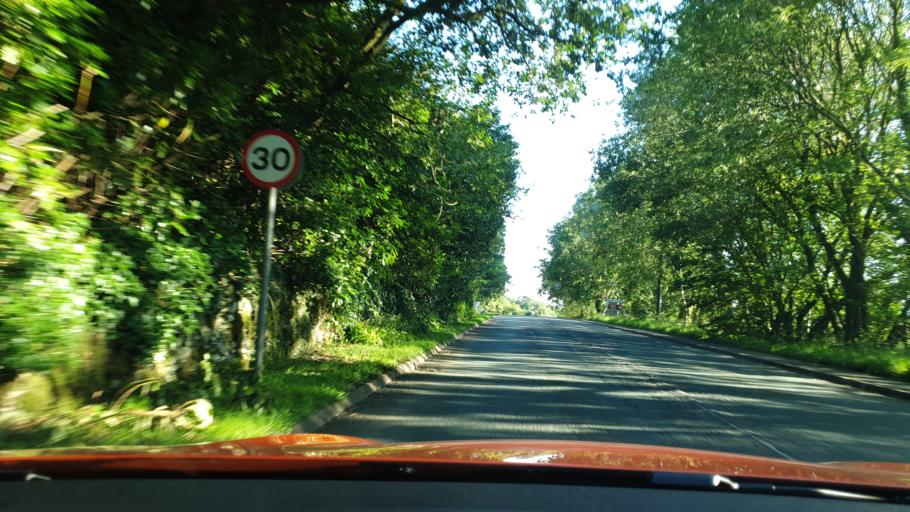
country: GB
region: England
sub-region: Cumbria
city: Windermere
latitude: 54.3965
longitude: -2.9147
